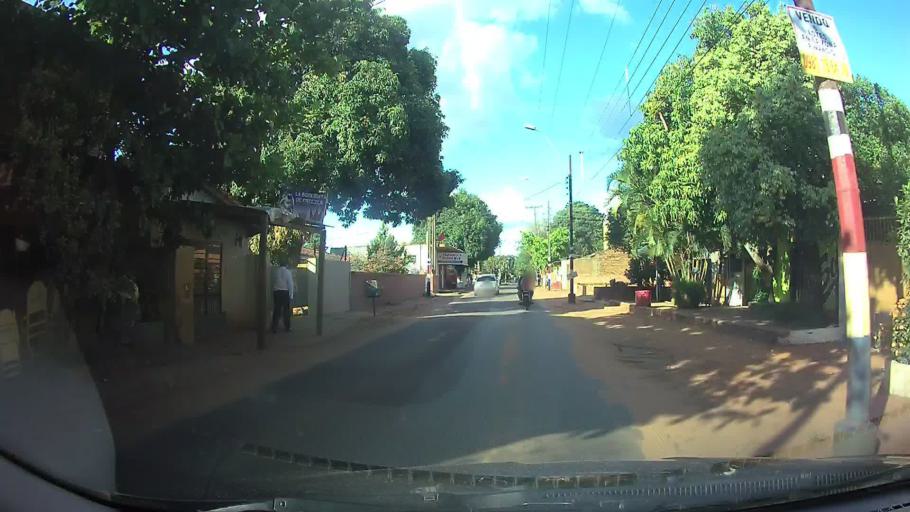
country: PY
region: Central
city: Aregua
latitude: -25.2880
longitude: -57.4394
